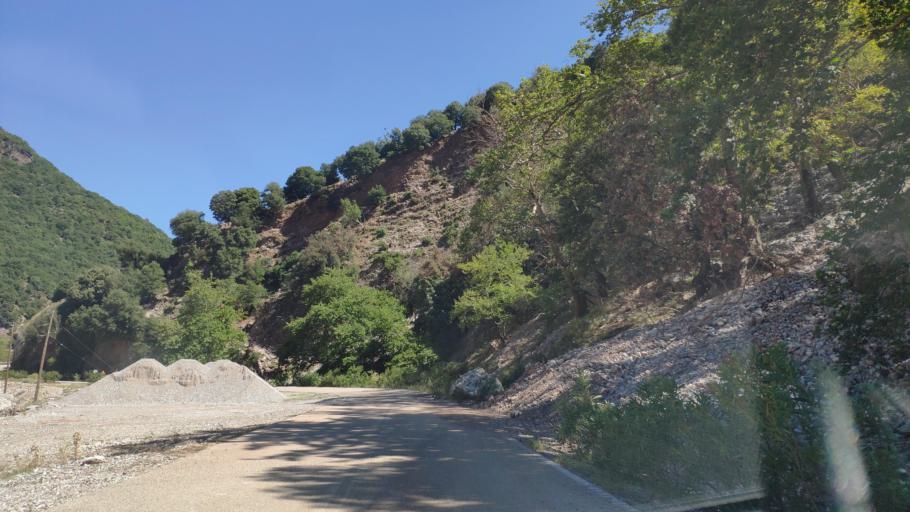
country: GR
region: Central Greece
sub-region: Nomos Evrytanias
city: Kerasochori
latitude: 39.0511
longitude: 21.6025
